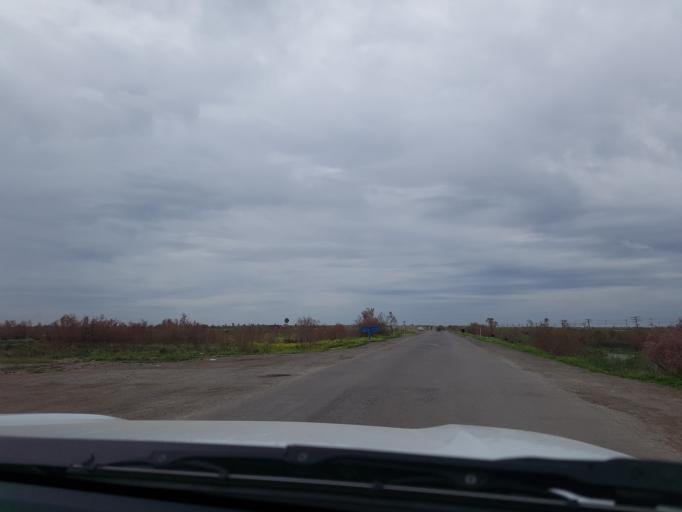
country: TM
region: Mary
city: Bayramaly
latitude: 37.7485
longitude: 62.4848
